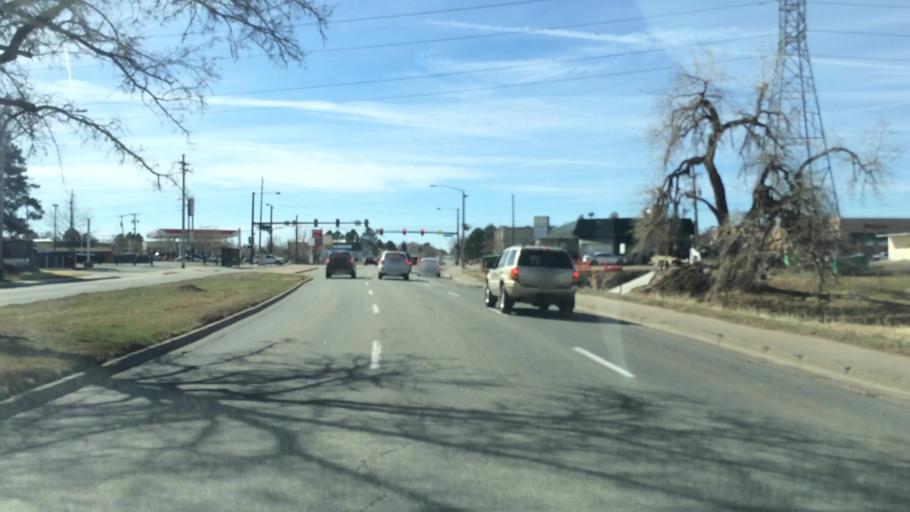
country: US
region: Colorado
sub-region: Arapahoe County
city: Glendale
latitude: 39.6798
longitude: -104.9130
